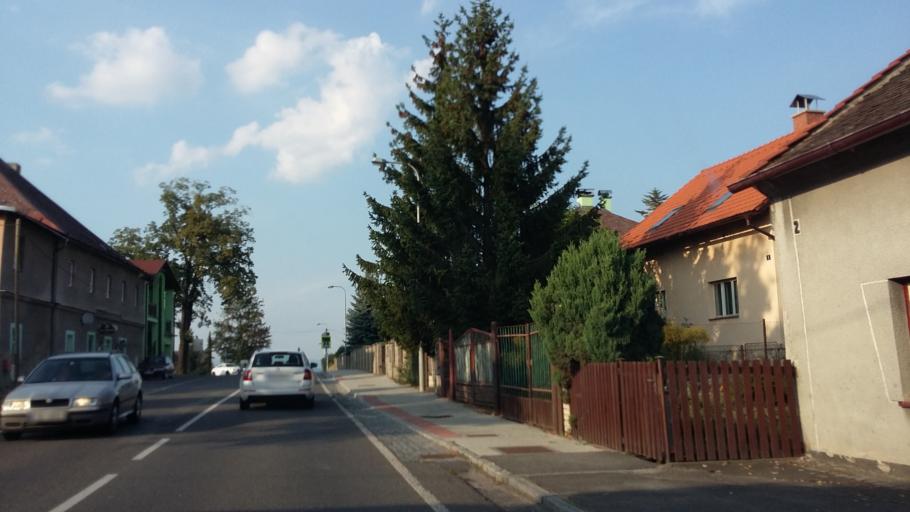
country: CZ
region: Central Bohemia
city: Kosmonosy
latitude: 50.4579
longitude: 14.9308
